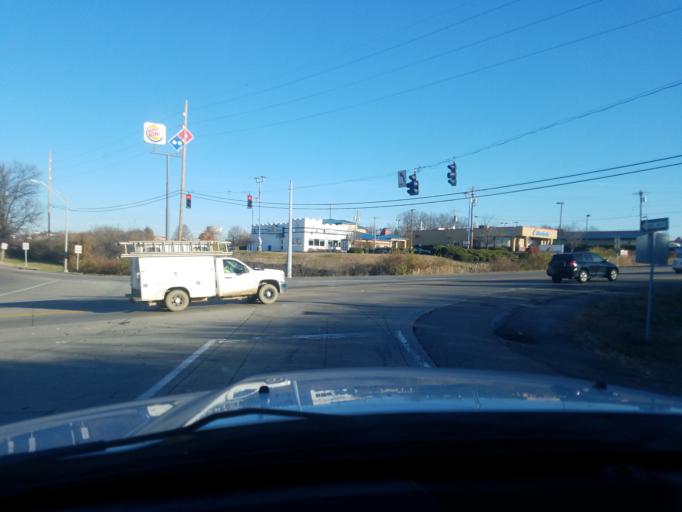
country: US
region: Kentucky
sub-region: Boone County
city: Walton
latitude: 38.9176
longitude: -84.6278
